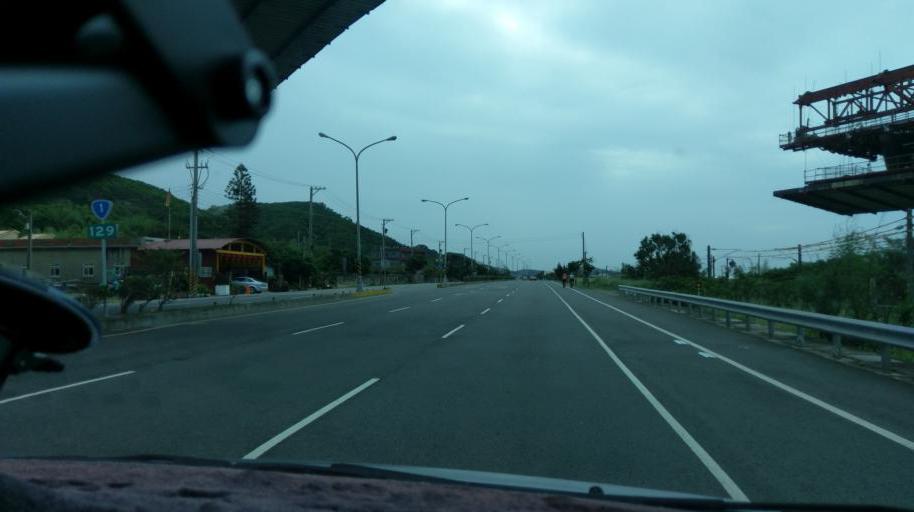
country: TW
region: Taiwan
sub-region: Miaoli
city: Miaoli
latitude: 24.5303
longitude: 120.6933
